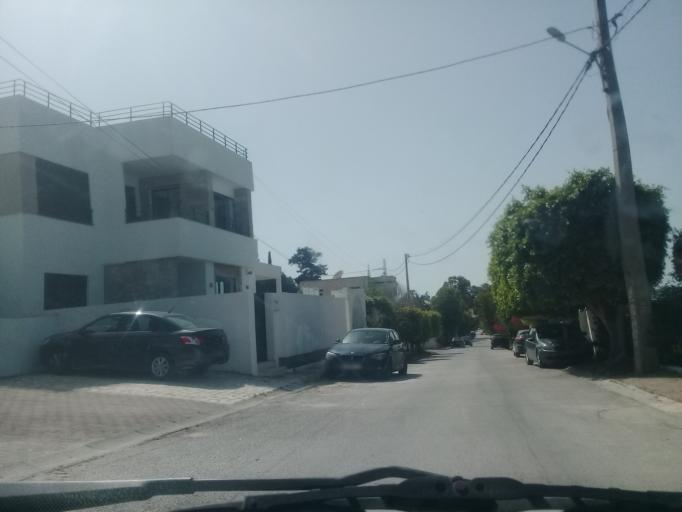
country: TN
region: Tunis
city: Sidi Bou Said
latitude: 36.8806
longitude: 10.3406
